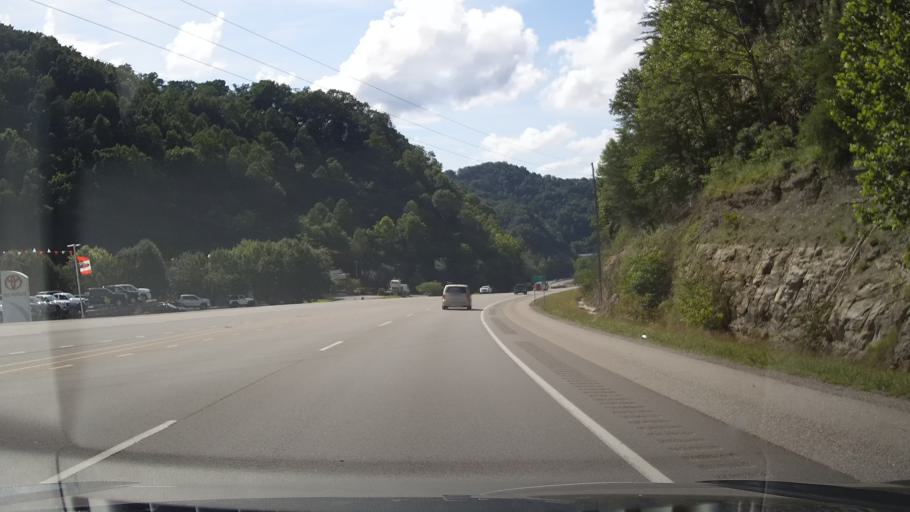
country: US
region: Kentucky
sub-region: Floyd County
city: Prestonsburg
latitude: 37.6448
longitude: -82.7764
